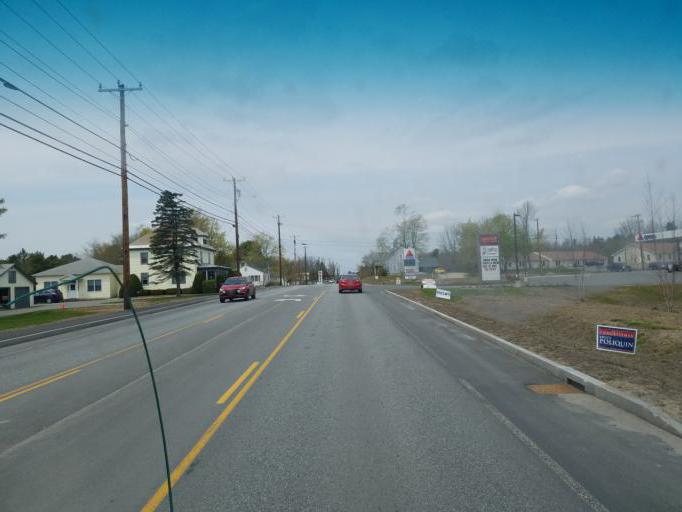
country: US
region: Maine
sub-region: Hancock County
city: Ellsworth
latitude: 44.5579
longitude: -68.4344
